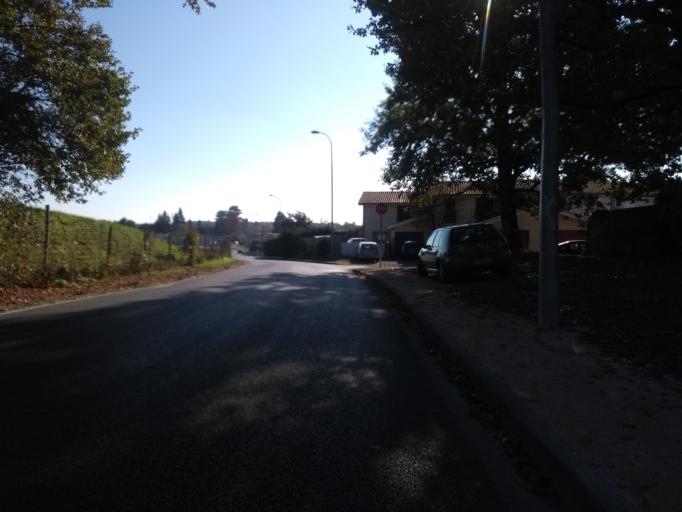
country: FR
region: Aquitaine
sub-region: Departement de la Gironde
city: Leognan
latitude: 44.7262
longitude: -0.5941
